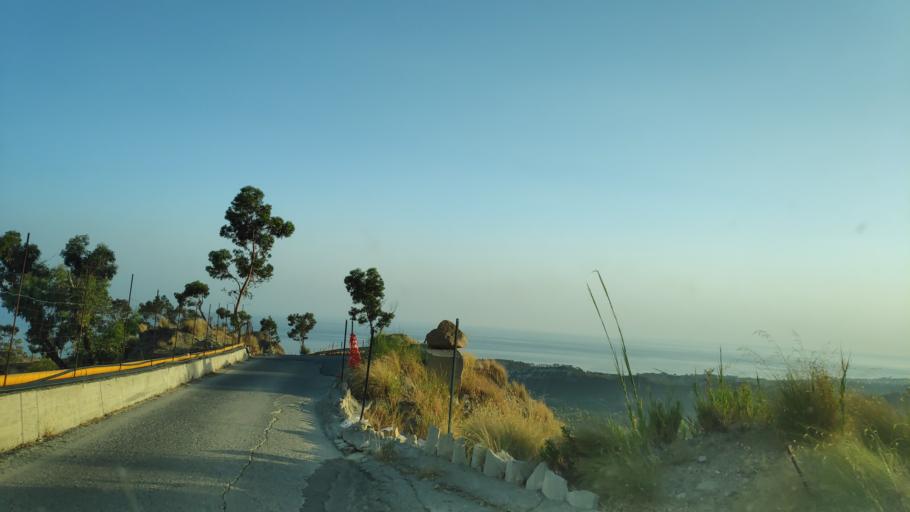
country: IT
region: Calabria
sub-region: Provincia di Reggio Calabria
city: Bova Marina
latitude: 37.9543
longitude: 15.9209
